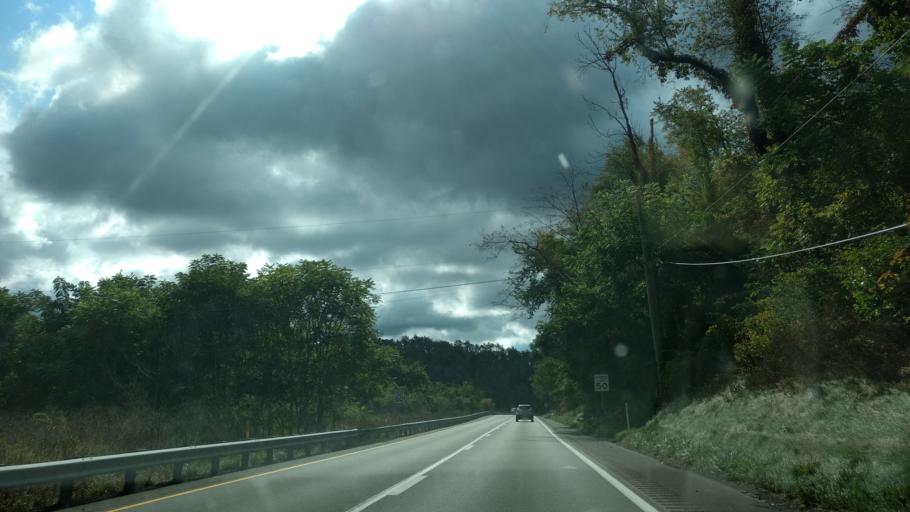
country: US
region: Pennsylvania
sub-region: Westmoreland County
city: Fellsburg
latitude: 40.1930
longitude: -79.8235
